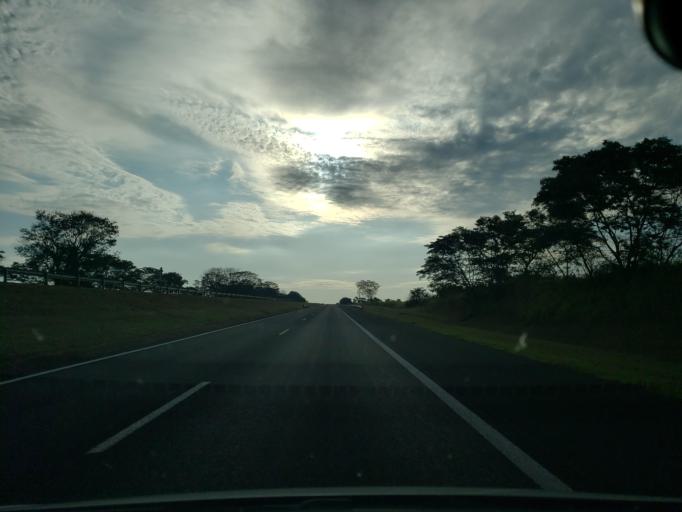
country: BR
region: Sao Paulo
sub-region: Mirandopolis
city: Mirandopolis
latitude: -21.0973
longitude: -51.0451
